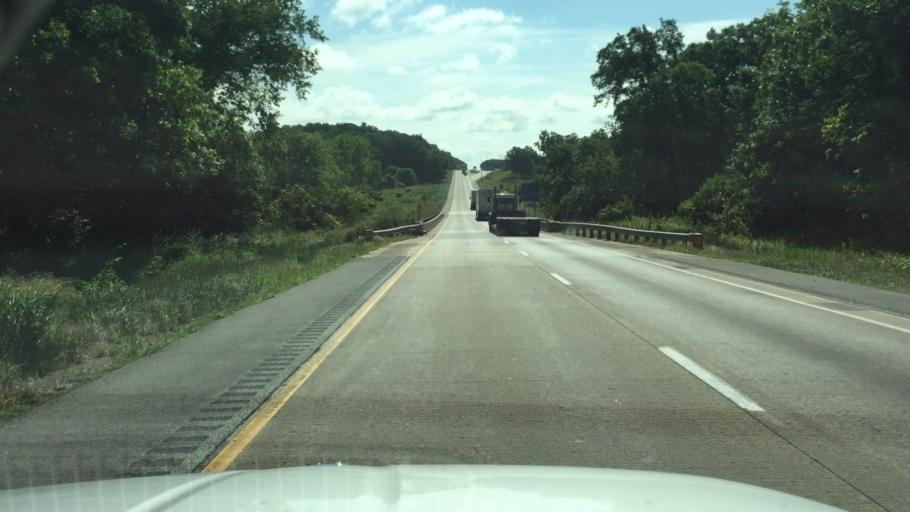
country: US
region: Iowa
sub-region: Muscatine County
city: Wilton
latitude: 41.6420
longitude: -91.0646
